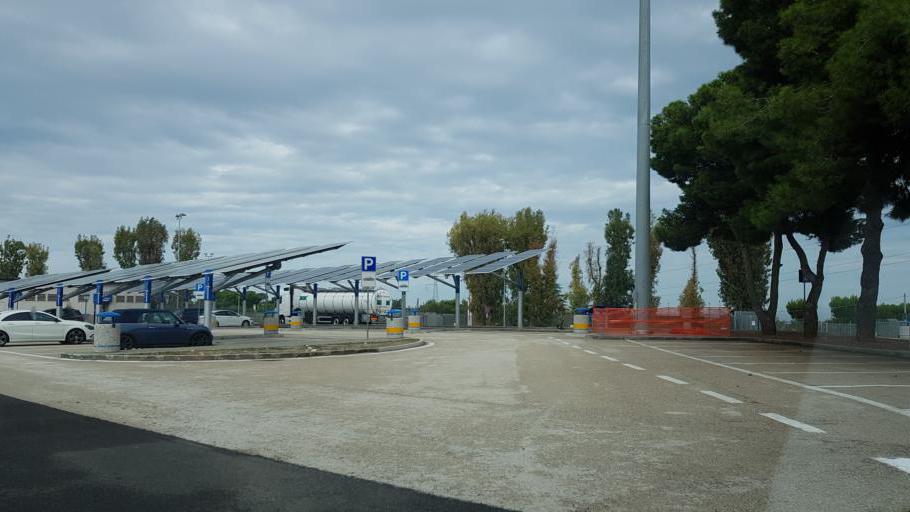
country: IT
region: Apulia
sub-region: Provincia di Barletta - Andria - Trani
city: Bisceglie
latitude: 41.1936
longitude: 16.4820
